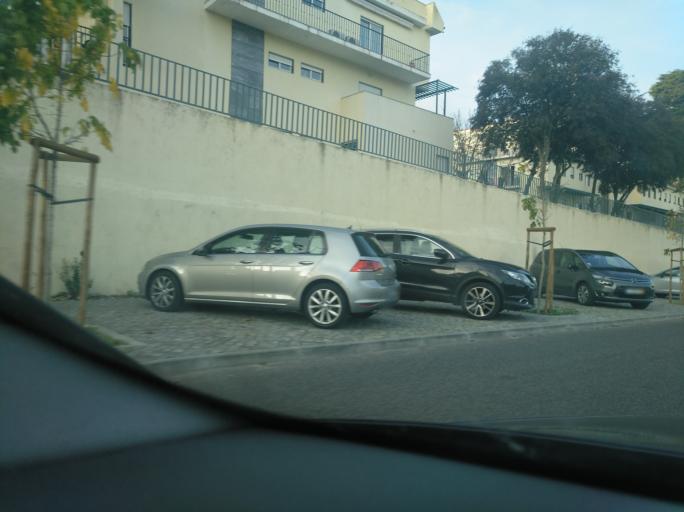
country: PT
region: Lisbon
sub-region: Odivelas
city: Olival do Basto
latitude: 38.7720
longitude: -9.1713
